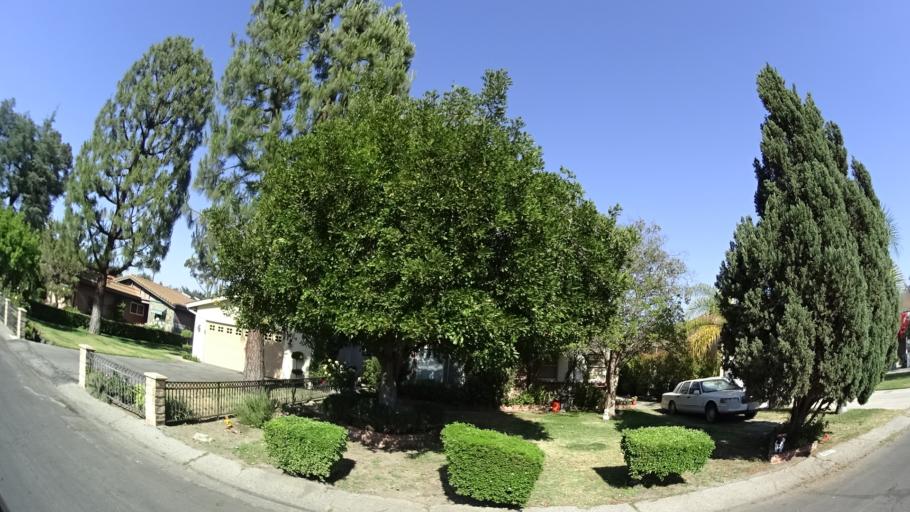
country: US
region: California
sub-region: Los Angeles County
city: North Hollywood
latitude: 34.1536
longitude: -118.3900
